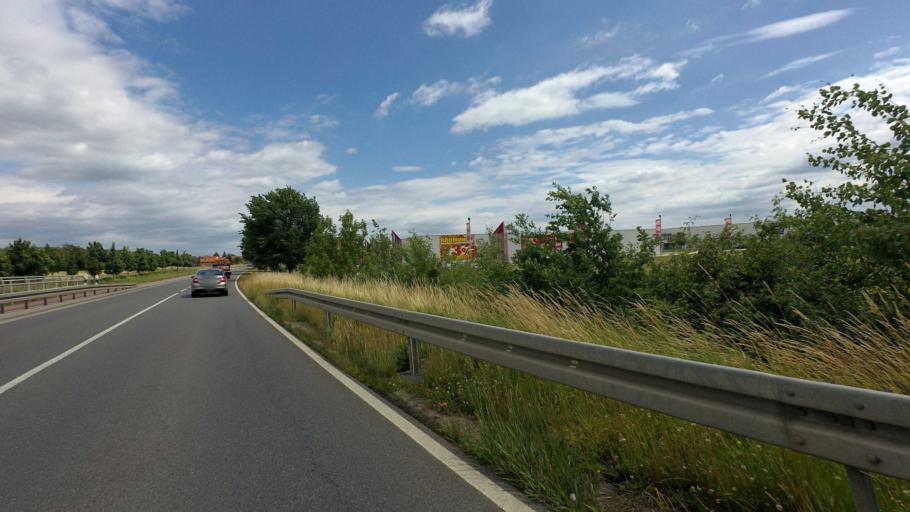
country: DE
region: Brandenburg
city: Grossraschen
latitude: 51.5829
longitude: 14.0230
